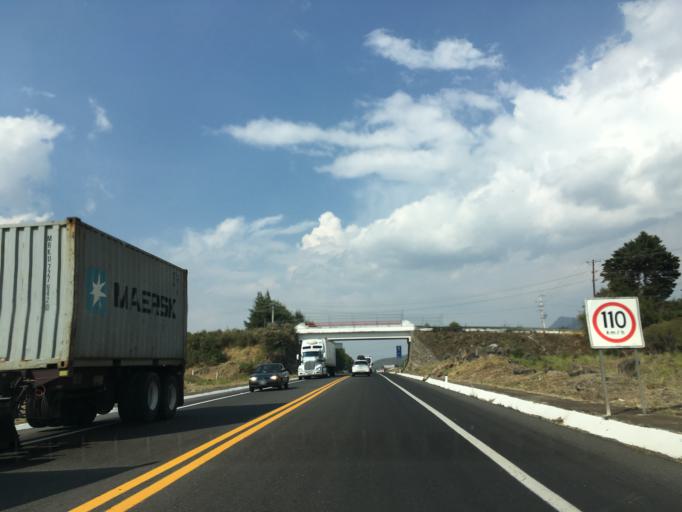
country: MX
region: Michoacan
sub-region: Patzcuaro
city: Colonia Vista Bella (Lomas del Peaje)
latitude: 19.4967
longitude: -101.5925
